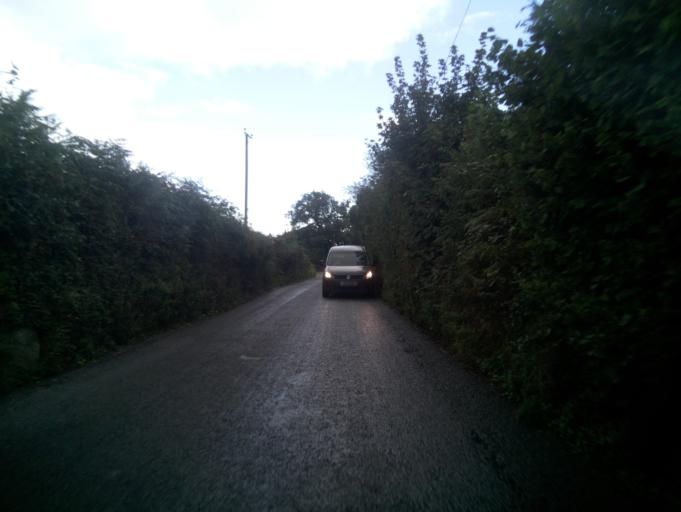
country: GB
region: England
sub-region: Devon
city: Ivybridge
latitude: 50.3806
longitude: -3.9213
